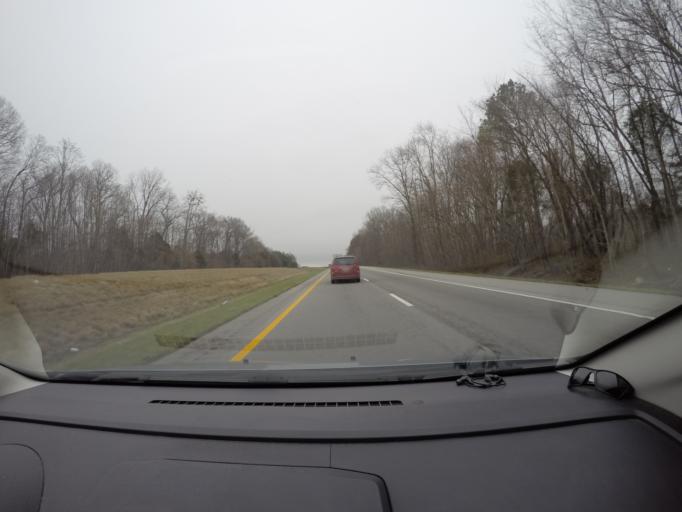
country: US
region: Tennessee
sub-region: Coffee County
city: Manchester
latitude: 35.3668
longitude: -85.9655
